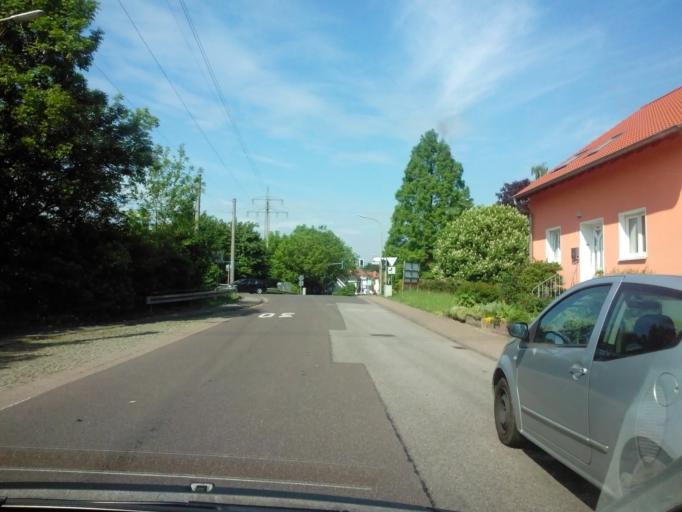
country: DE
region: Saarland
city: Schmelz
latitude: 49.3919
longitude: 6.8383
